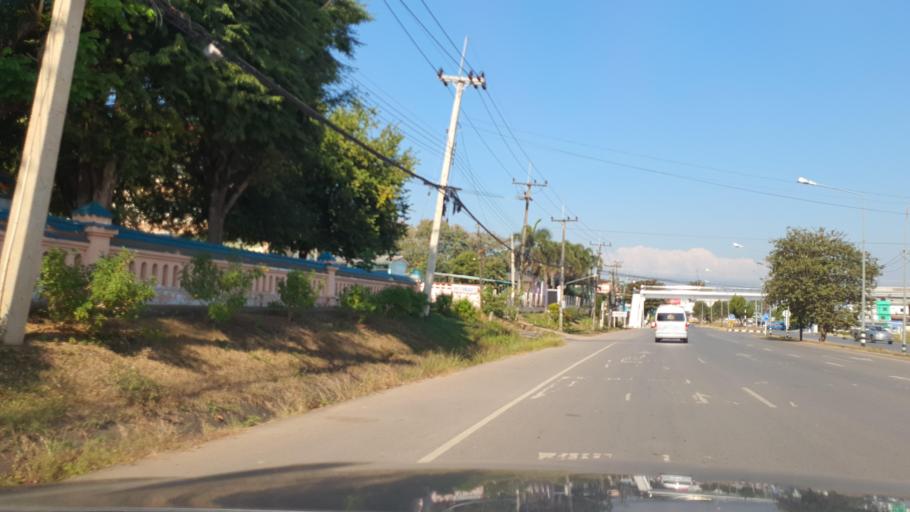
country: TH
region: Nan
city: Pua
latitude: 19.1750
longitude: 100.9169
